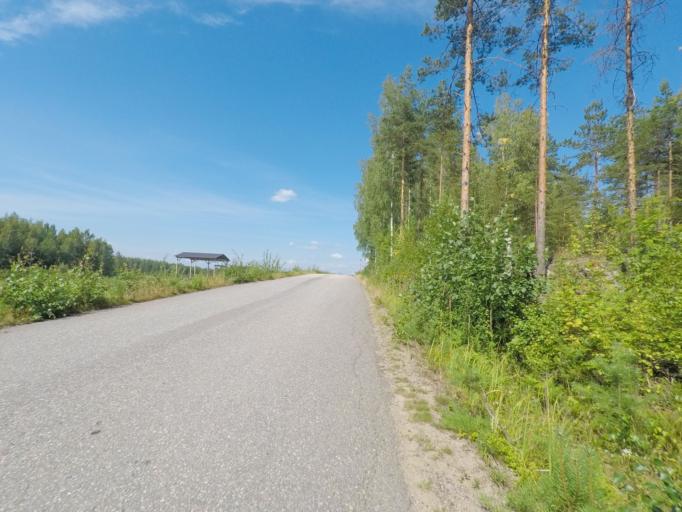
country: FI
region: Southern Savonia
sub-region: Mikkeli
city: Puumala
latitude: 61.4134
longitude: 28.0921
